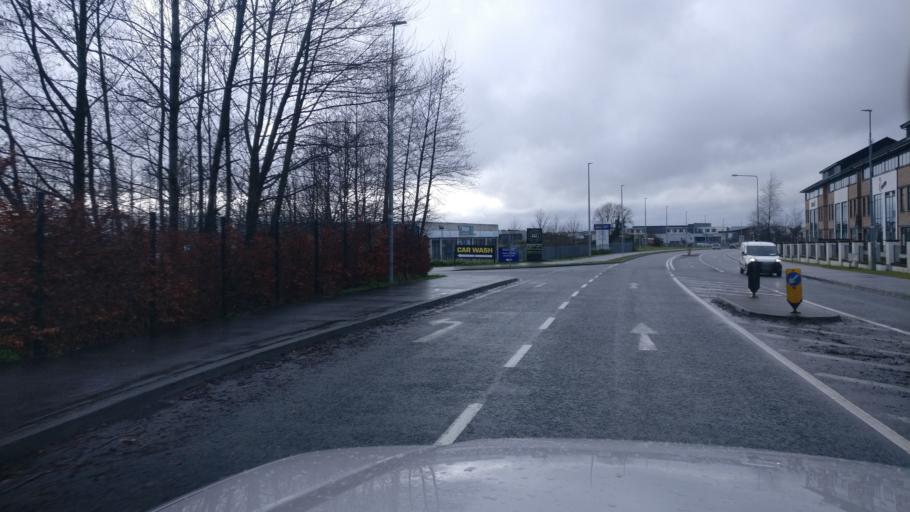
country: IE
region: Leinster
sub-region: An Iarmhi
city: Athlone
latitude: 53.4206
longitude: -7.9898
